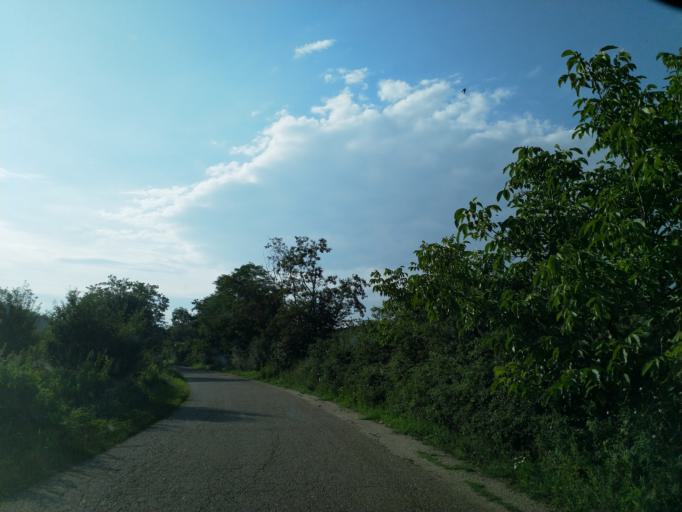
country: RS
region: Central Serbia
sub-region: Pomoravski Okrug
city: Jagodina
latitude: 44.0014
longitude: 21.1870
